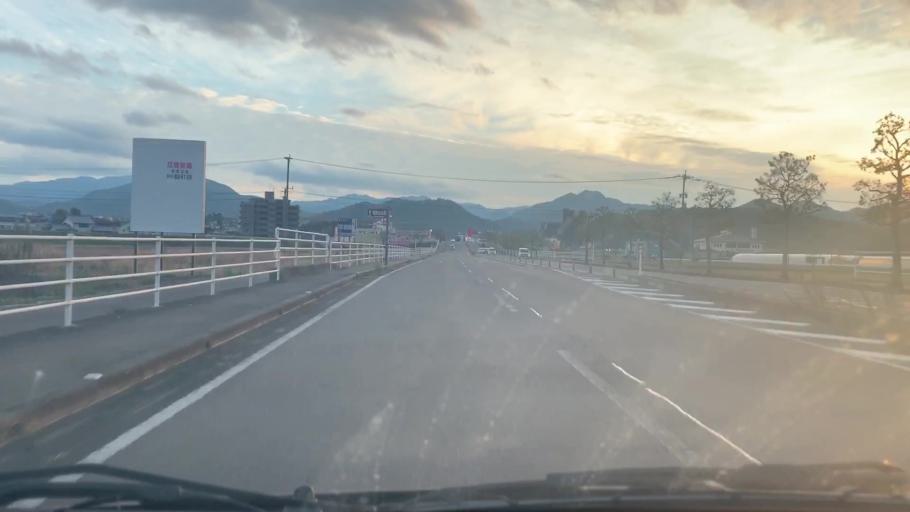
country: JP
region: Saga Prefecture
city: Kashima
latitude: 33.1163
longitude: 130.0892
